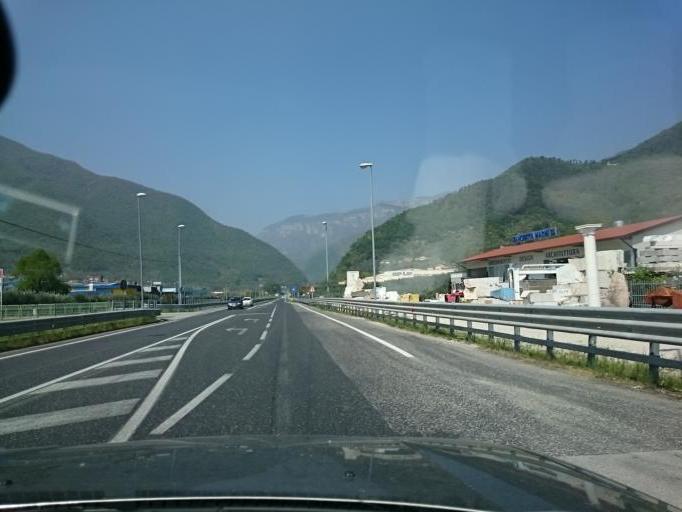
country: IT
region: Veneto
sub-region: Provincia di Vicenza
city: Pove del Grappa
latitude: 45.7973
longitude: 11.7218
